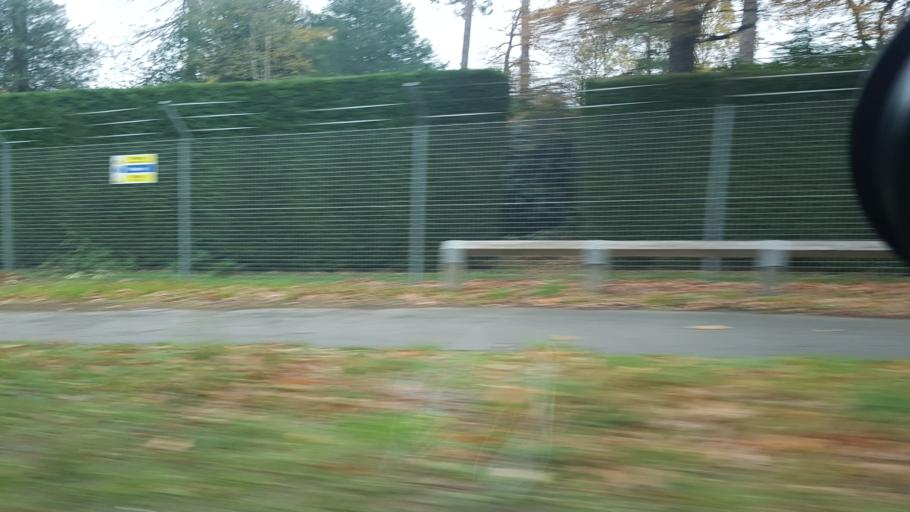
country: GB
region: England
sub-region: Hampshire
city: Yateley
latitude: 51.3173
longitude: -0.8199
